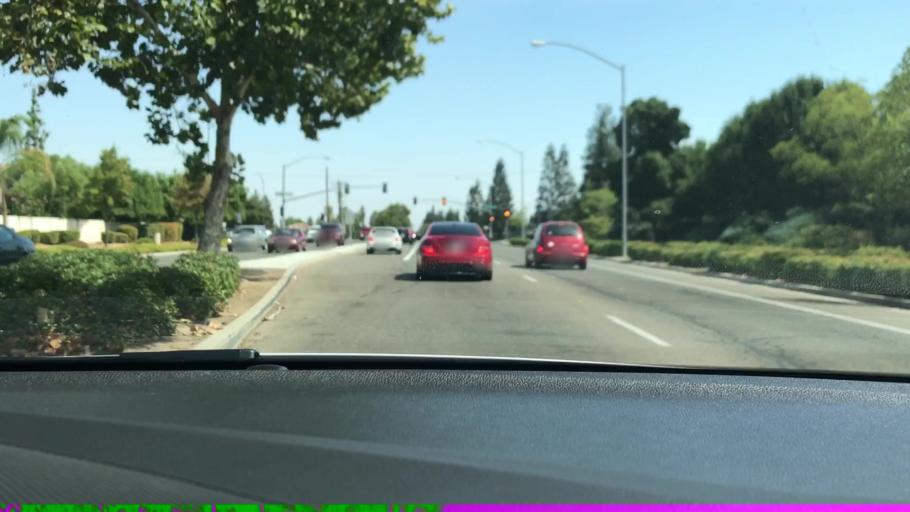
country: US
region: California
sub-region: Fresno County
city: Clovis
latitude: 36.8519
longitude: -119.7672
